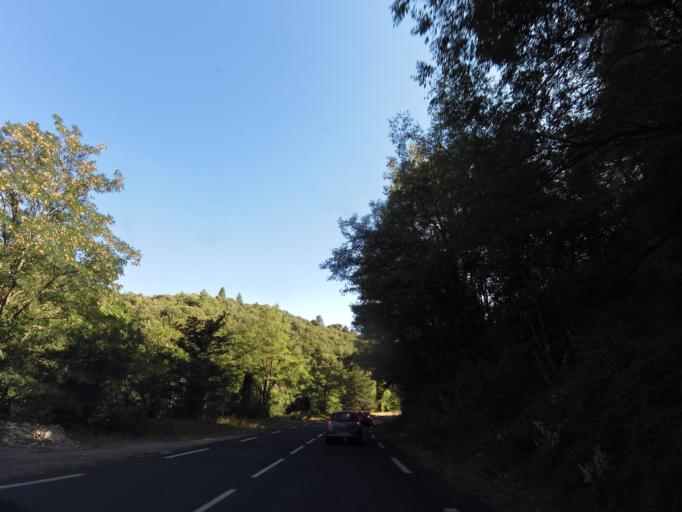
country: FR
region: Languedoc-Roussillon
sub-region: Departement du Gard
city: Valleraugue
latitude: 44.0437
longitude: 3.6754
